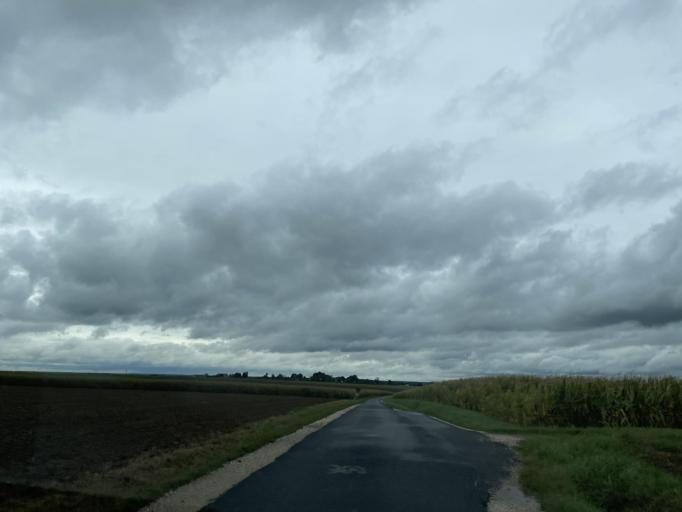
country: FR
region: Ile-de-France
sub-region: Departement de Seine-et-Marne
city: Chailly-en-Brie
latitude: 48.7885
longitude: 3.1565
